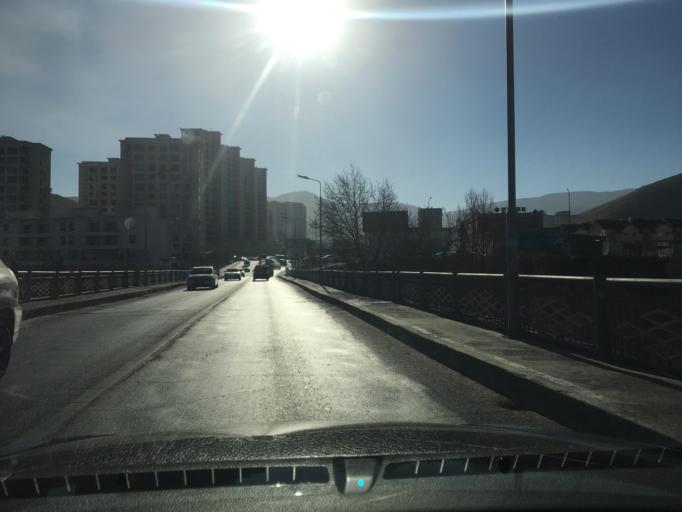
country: MN
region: Ulaanbaatar
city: Ulaanbaatar
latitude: 47.8898
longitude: 106.9099
